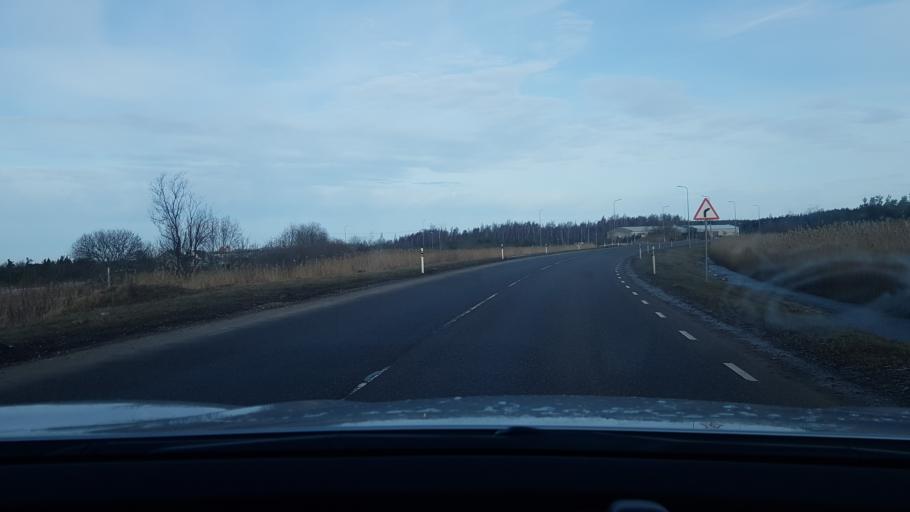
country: EE
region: Saare
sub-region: Kuressaare linn
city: Kuressaare
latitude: 58.2350
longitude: 22.5008
